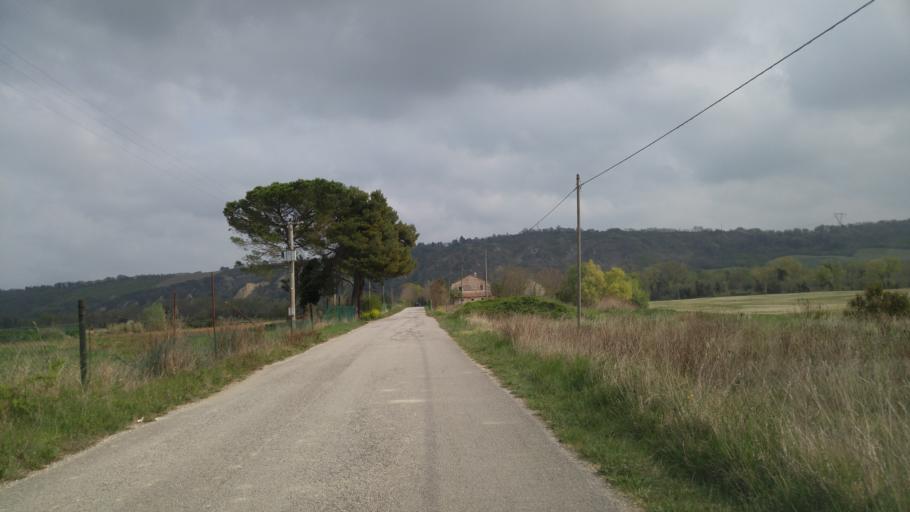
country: IT
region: The Marches
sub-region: Provincia di Pesaro e Urbino
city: Bellocchi
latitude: 43.7749
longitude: 12.9843
